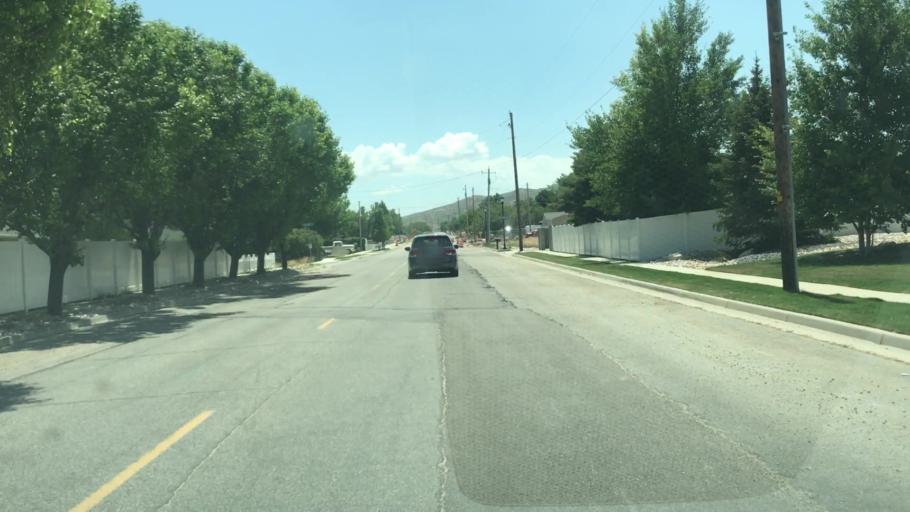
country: US
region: Utah
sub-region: Salt Lake County
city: Bluffdale
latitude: 40.4830
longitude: -111.9484
